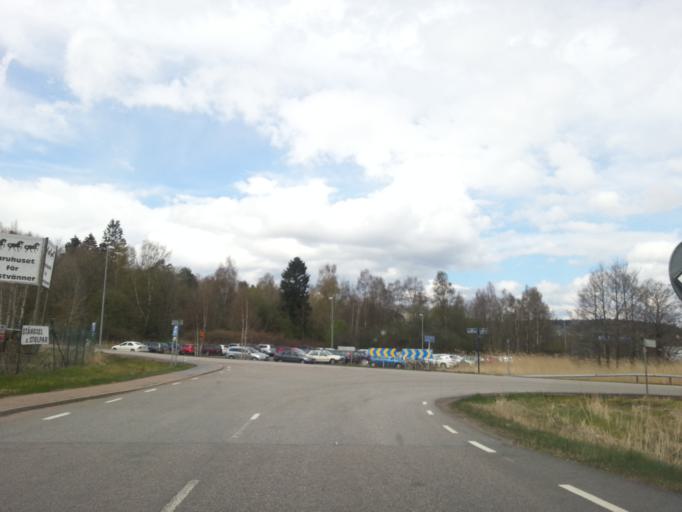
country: SE
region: Vaestra Goetaland
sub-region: Kungalvs Kommun
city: Kungalv
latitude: 57.8544
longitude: 12.0006
